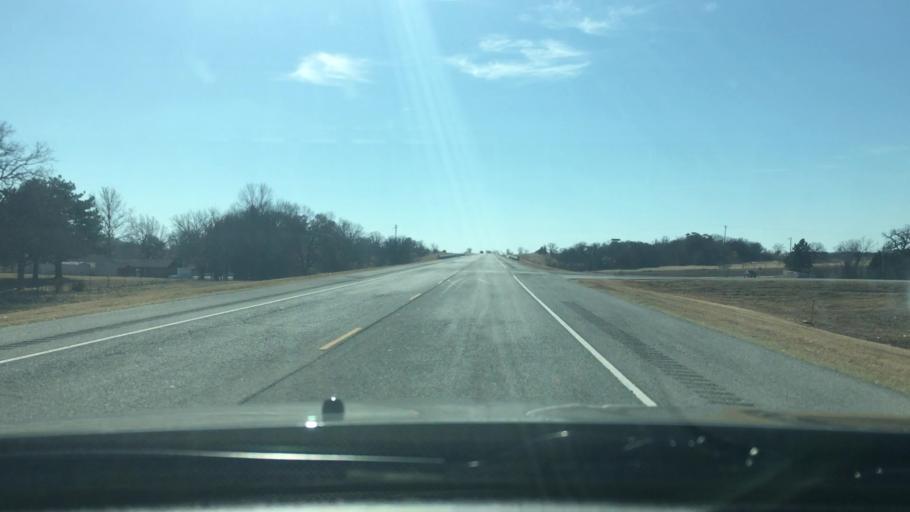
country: US
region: Oklahoma
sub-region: Stephens County
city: Meridian
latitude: 34.4077
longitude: -97.9742
